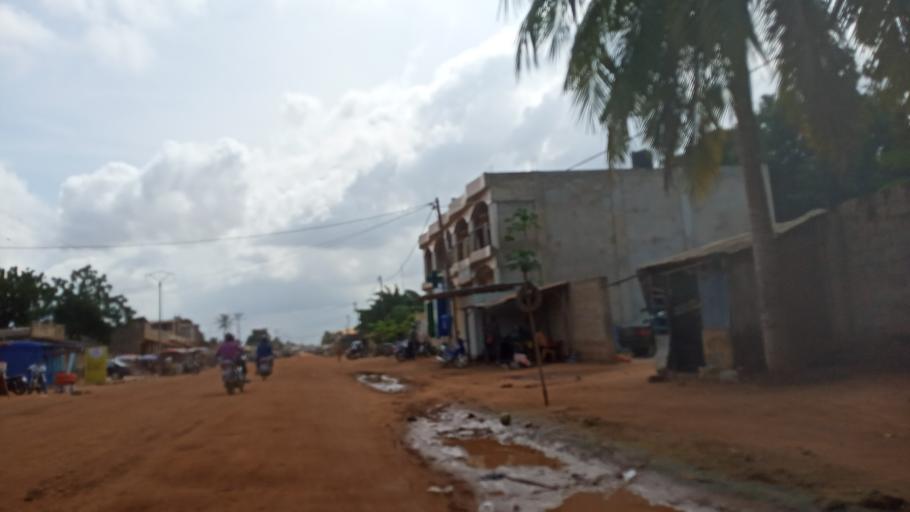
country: TG
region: Maritime
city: Lome
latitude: 6.2334
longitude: 1.1487
